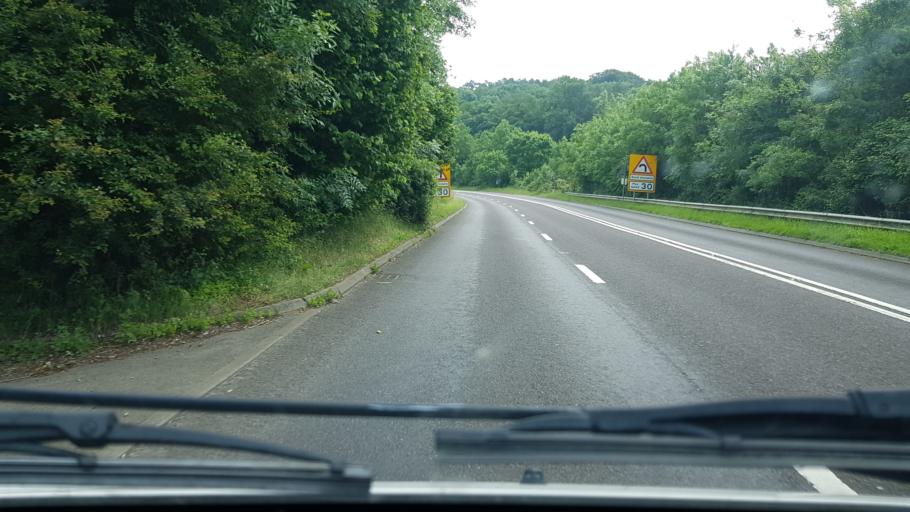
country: GB
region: England
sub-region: Worcestershire
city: Broadway
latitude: 52.0327
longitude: -1.8401
